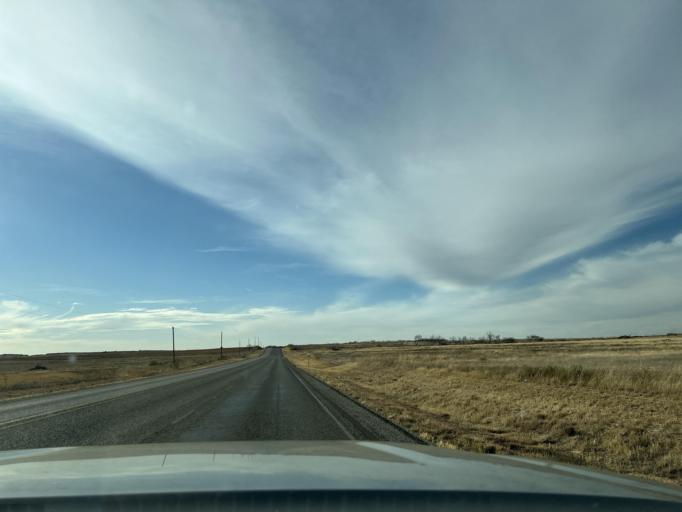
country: US
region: Texas
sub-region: Fisher County
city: Rotan
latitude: 32.7395
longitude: -100.5303
